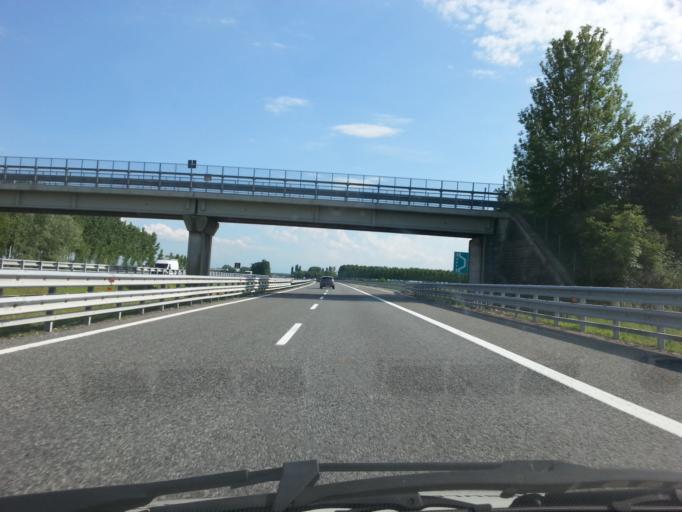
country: IT
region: Piedmont
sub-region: Provincia di Cuneo
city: Caramagna Piemonte
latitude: 44.7515
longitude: 7.7502
